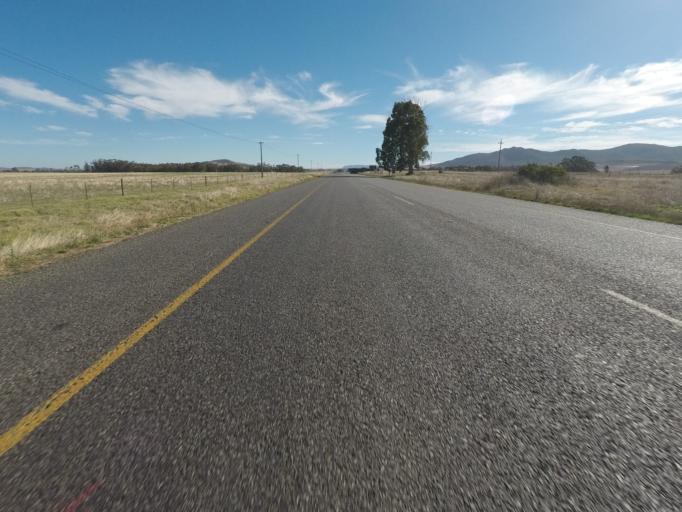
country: ZA
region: Western Cape
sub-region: West Coast District Municipality
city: Malmesbury
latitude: -33.6234
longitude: 18.7250
